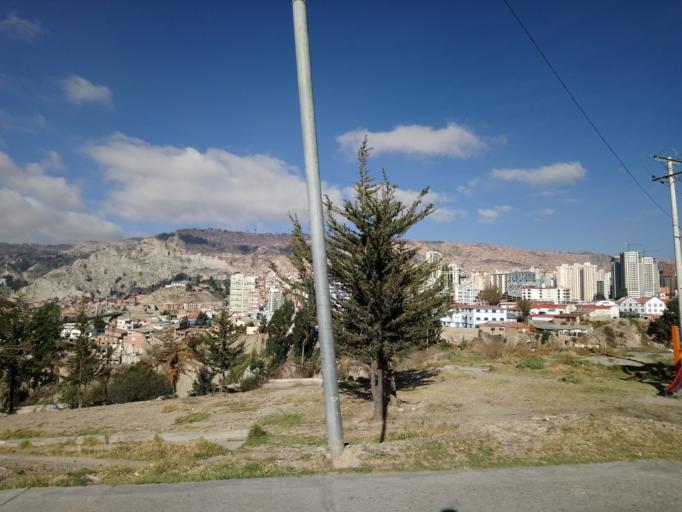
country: BO
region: La Paz
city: La Paz
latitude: -16.5121
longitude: -68.1146
